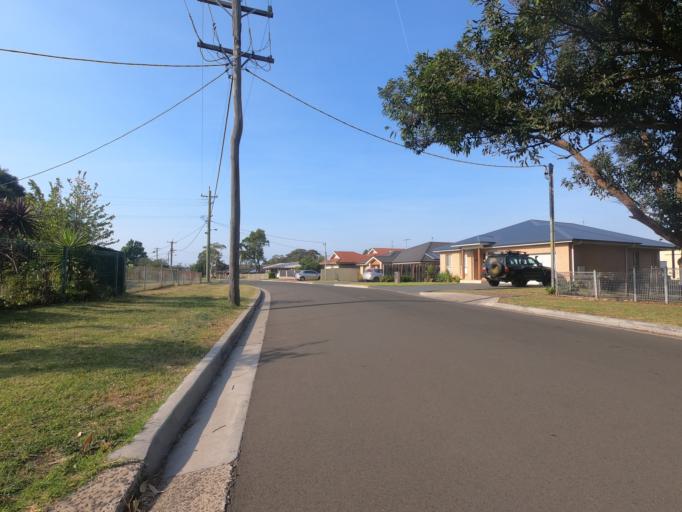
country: AU
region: New South Wales
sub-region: Wollongong
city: Berkeley
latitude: -34.4810
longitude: 150.8575
